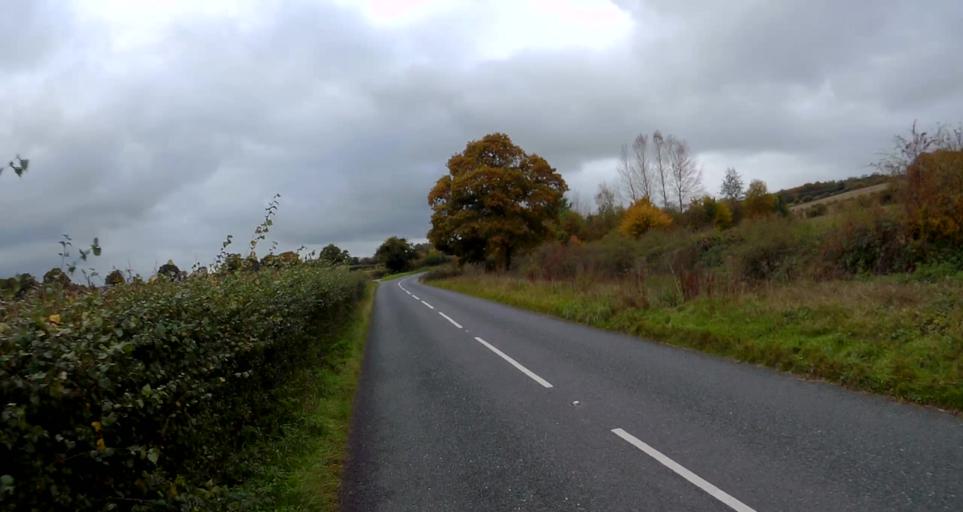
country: GB
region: England
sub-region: Hampshire
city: Four Marks
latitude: 51.1614
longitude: -1.1443
